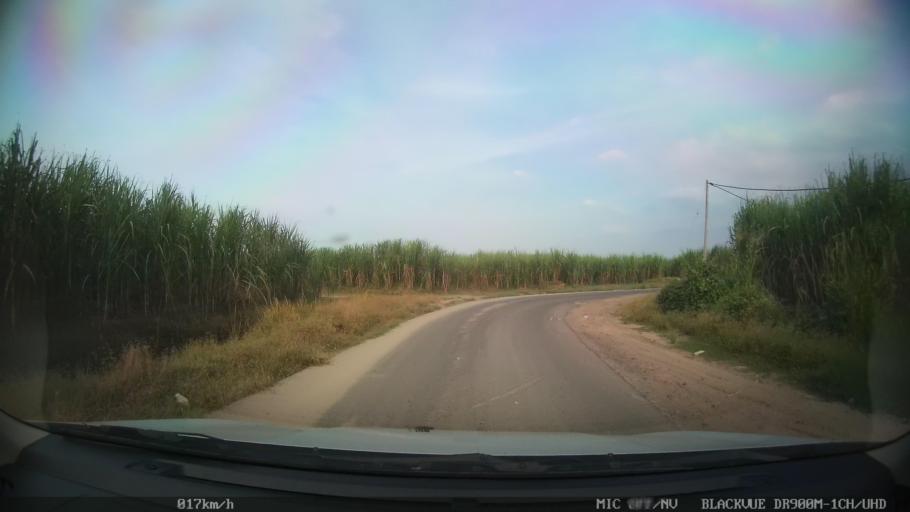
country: ID
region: North Sumatra
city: Binjai
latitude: 3.5927
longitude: 98.5409
